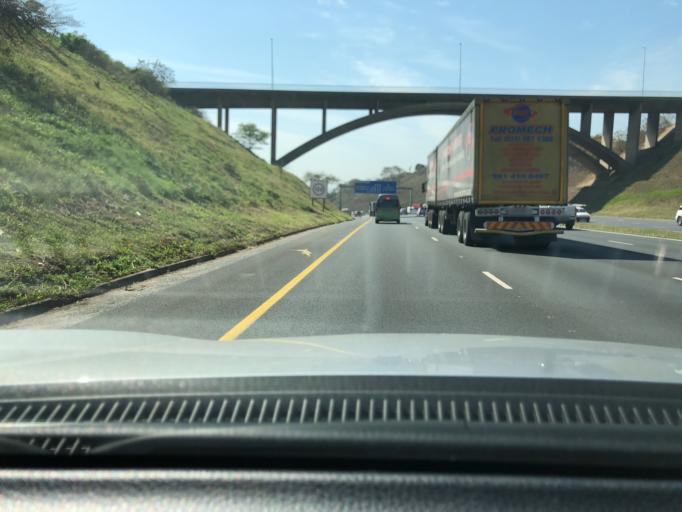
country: ZA
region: KwaZulu-Natal
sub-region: eThekwini Metropolitan Municipality
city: Berea
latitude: -29.8183
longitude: 30.9704
